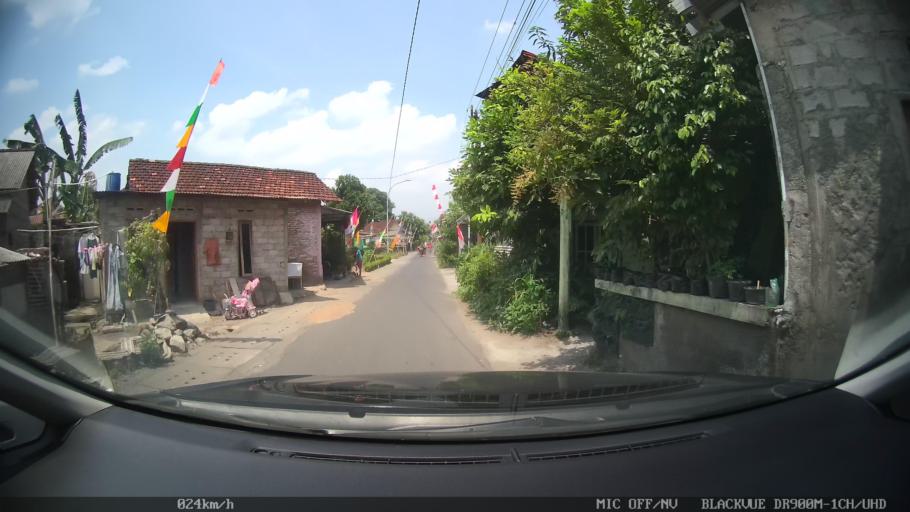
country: ID
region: Daerah Istimewa Yogyakarta
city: Yogyakarta
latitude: -7.8229
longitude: 110.4057
